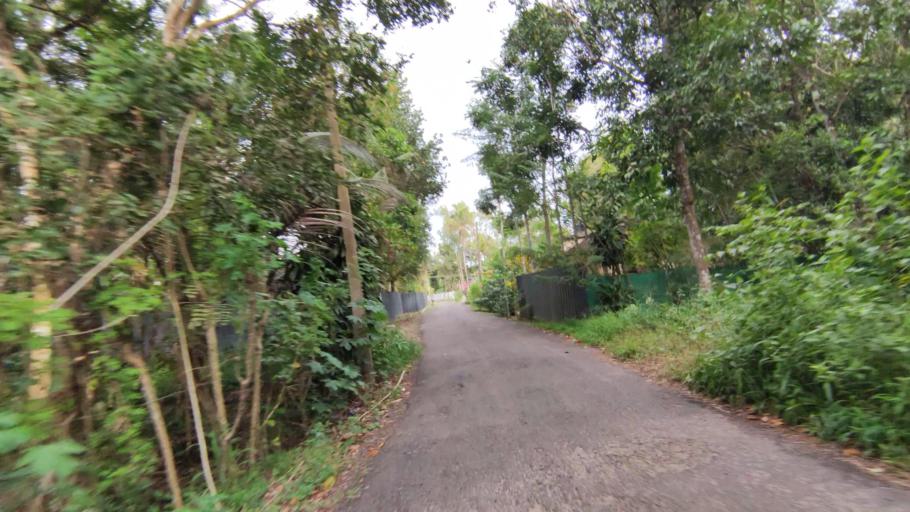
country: IN
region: Kerala
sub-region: Alappuzha
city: Shertallai
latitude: 9.6189
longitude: 76.3450
